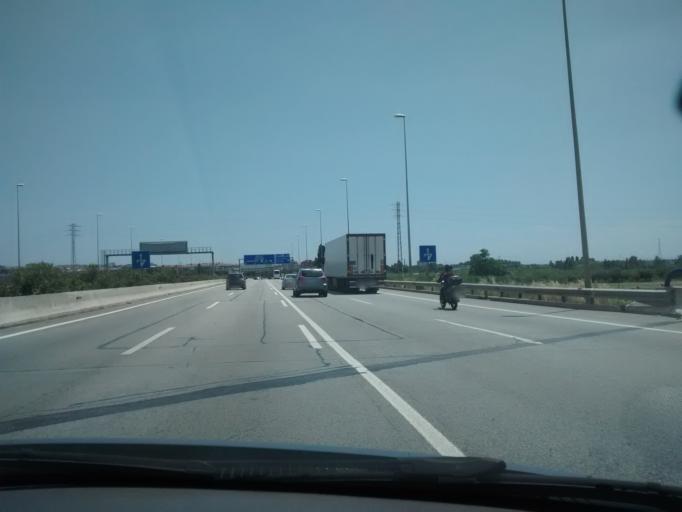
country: ES
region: Catalonia
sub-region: Provincia de Barcelona
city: Sant Feliu de Llobregat
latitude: 41.3698
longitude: 2.0412
